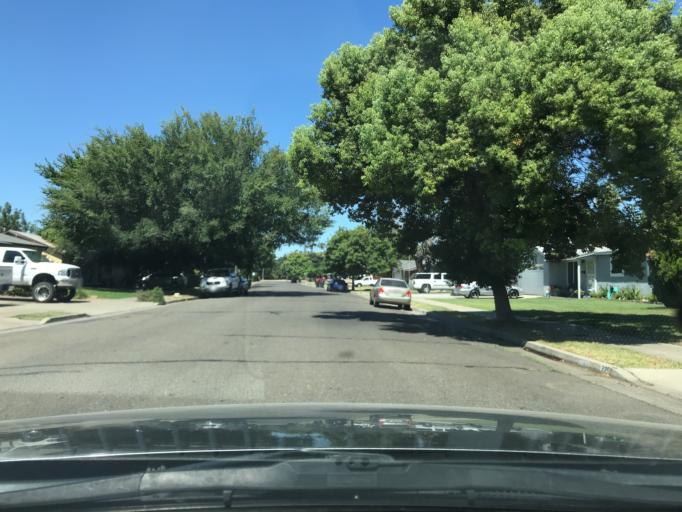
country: US
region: California
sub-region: Merced County
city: Atwater
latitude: 37.3452
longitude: -120.5930
